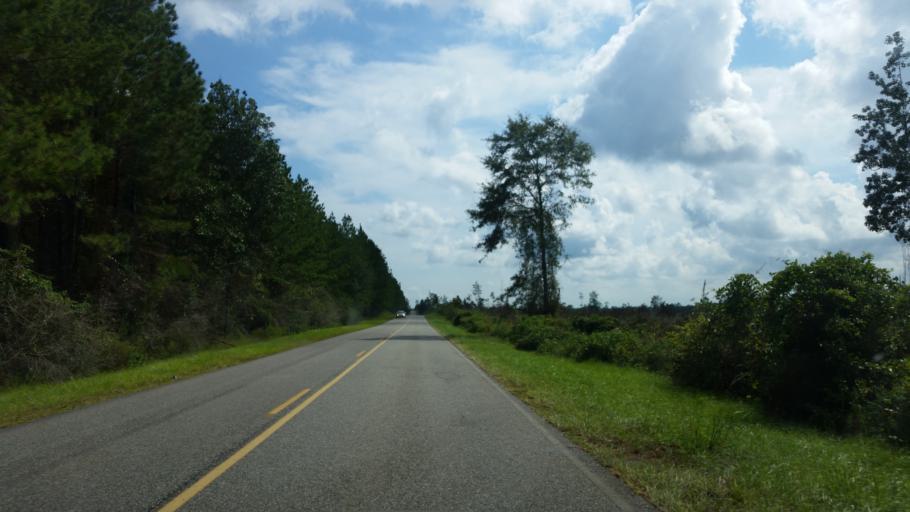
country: US
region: Florida
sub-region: Escambia County
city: Cantonment
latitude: 30.6884
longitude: -87.4558
